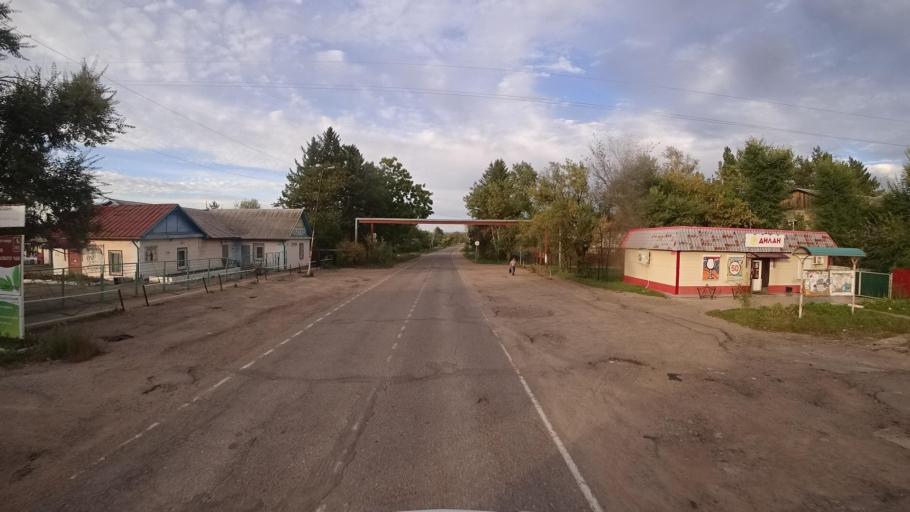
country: RU
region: Primorskiy
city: Yakovlevka
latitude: 44.4274
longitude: 133.4803
